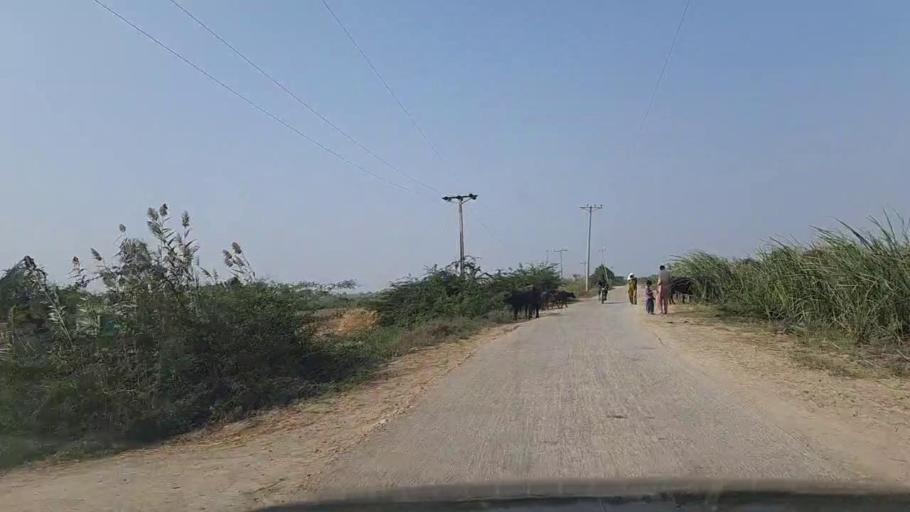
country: PK
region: Sindh
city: Thatta
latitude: 24.7385
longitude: 67.7599
